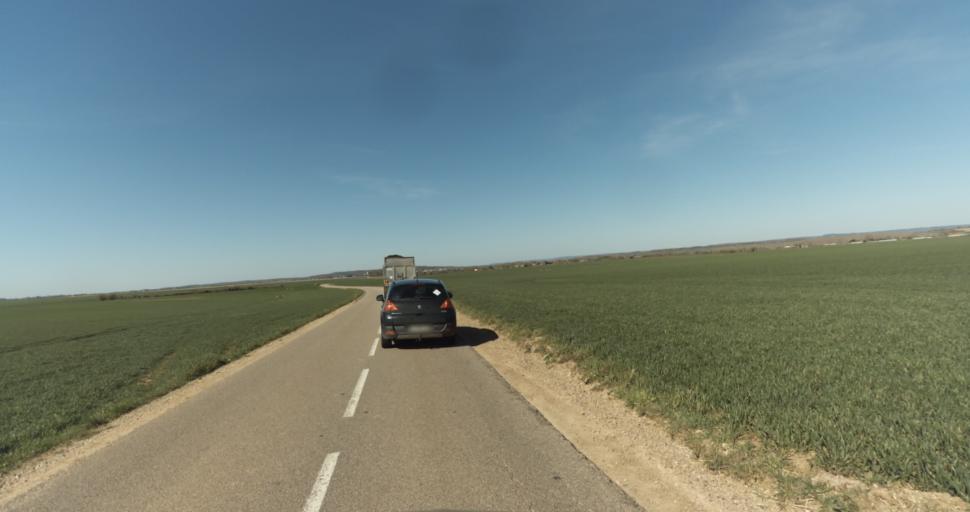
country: FR
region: Lower Normandy
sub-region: Departement du Calvados
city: Saint-Pierre-sur-Dives
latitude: 49.0383
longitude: -0.0651
